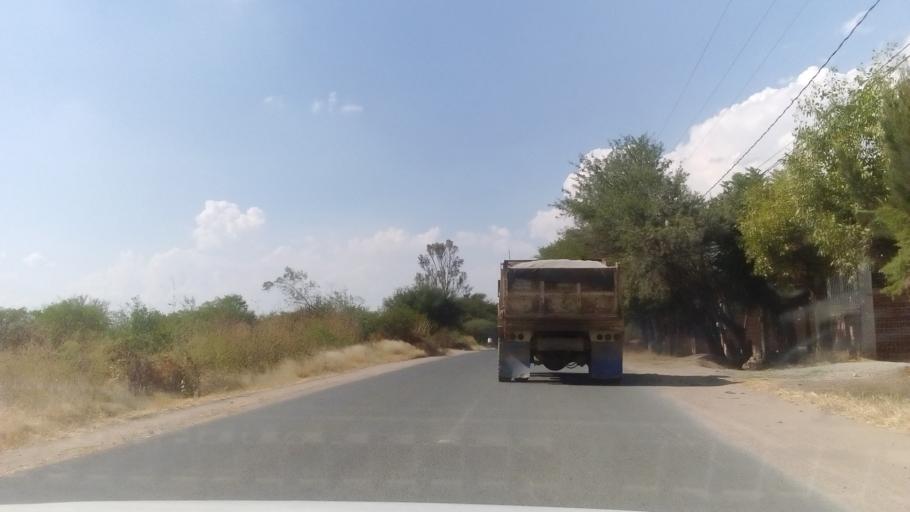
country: MX
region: Guanajuato
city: Duarte
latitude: 21.0898
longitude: -101.5343
